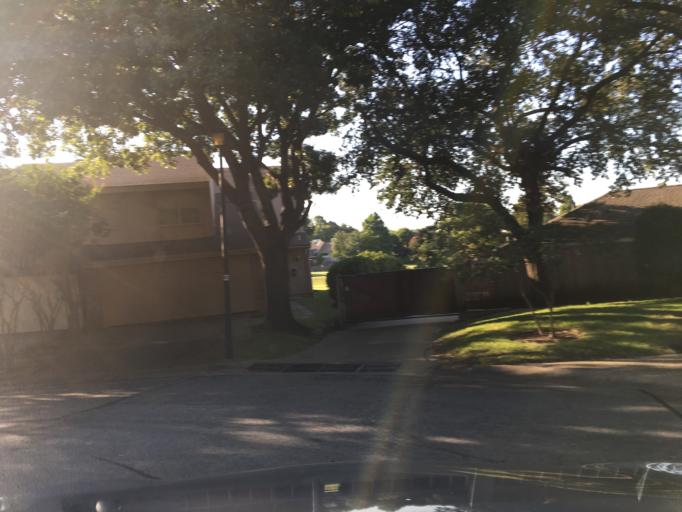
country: US
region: Texas
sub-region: Dallas County
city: Addison
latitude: 32.9634
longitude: -96.8573
